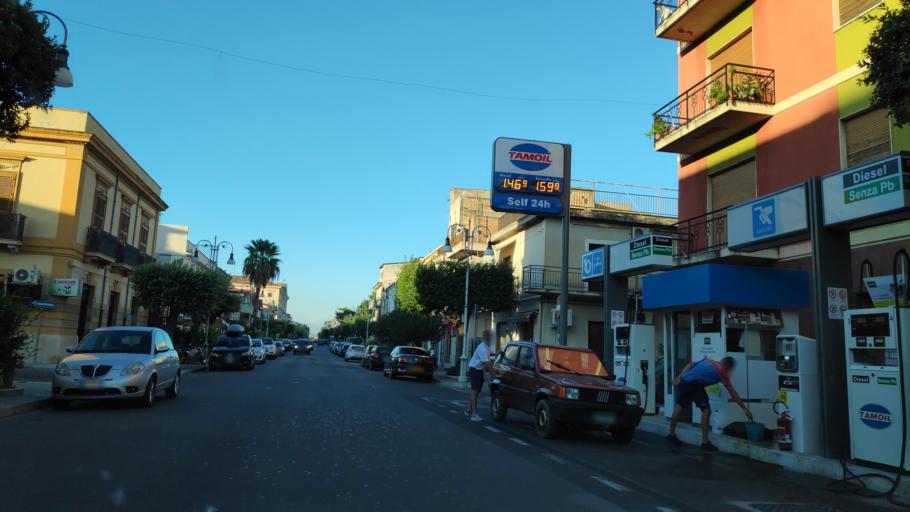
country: IT
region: Calabria
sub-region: Provincia di Reggio Calabria
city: Locri
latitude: 38.2351
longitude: 16.2629
